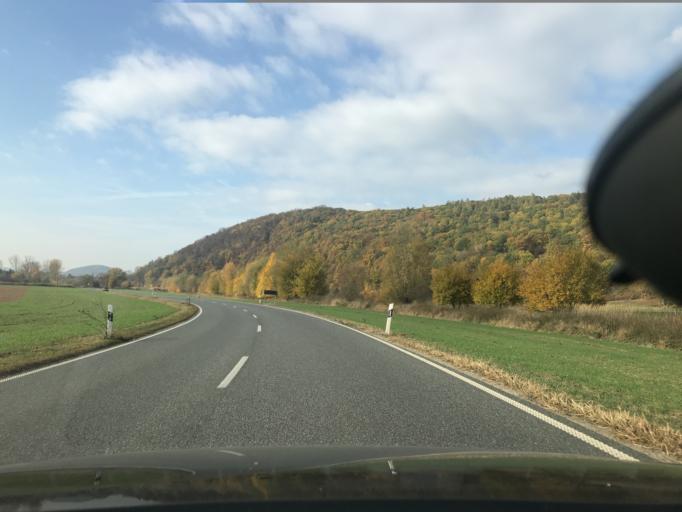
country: DE
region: Hesse
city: Wanfried
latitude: 51.1956
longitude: 10.1515
